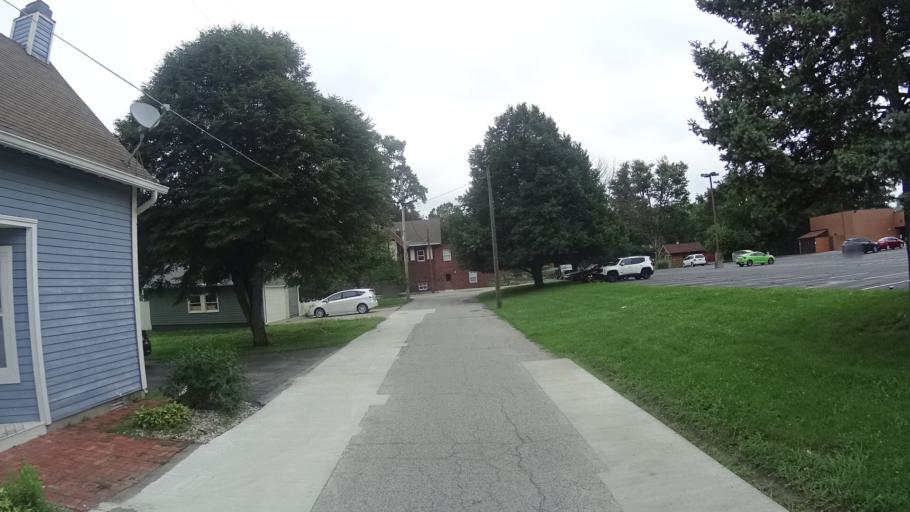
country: US
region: Indiana
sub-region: Madison County
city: Pendleton
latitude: 40.0012
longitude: -85.7413
